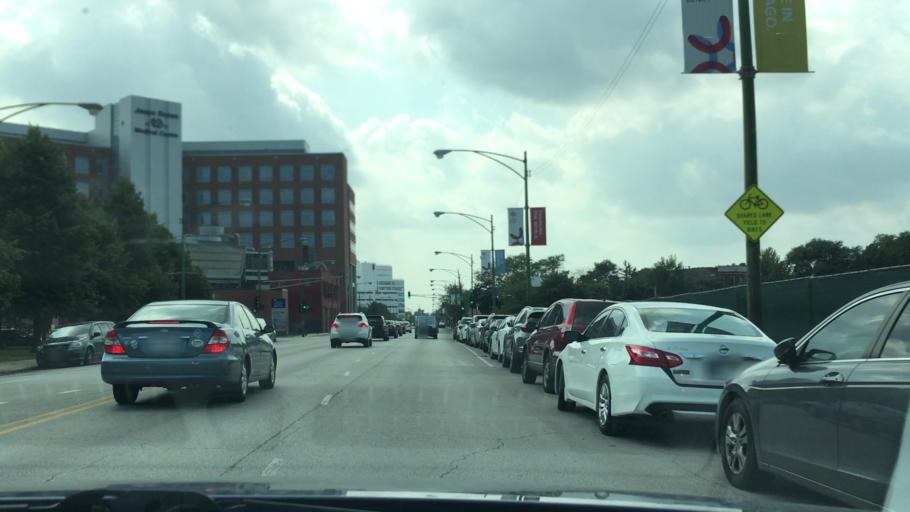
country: US
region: Illinois
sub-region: Cook County
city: Chicago
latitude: 41.8722
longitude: -87.6772
